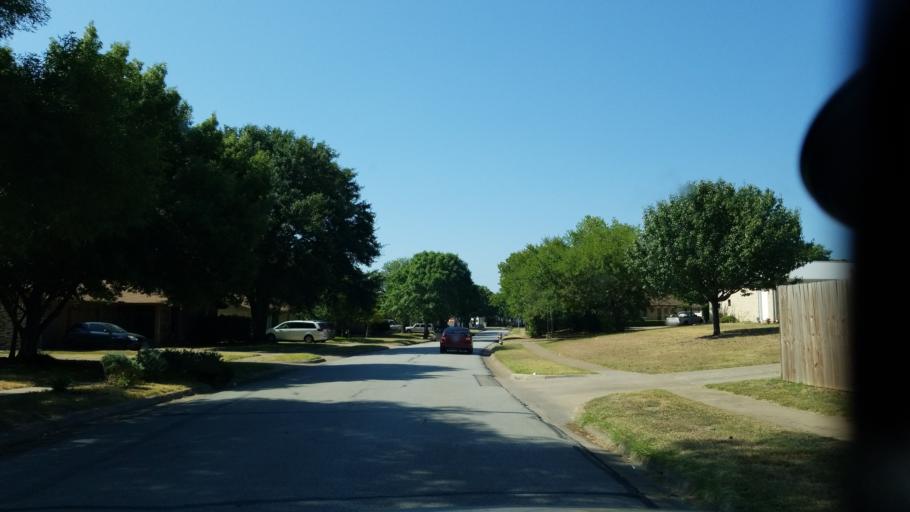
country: US
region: Texas
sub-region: Dallas County
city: Duncanville
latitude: 32.6369
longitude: -96.9004
